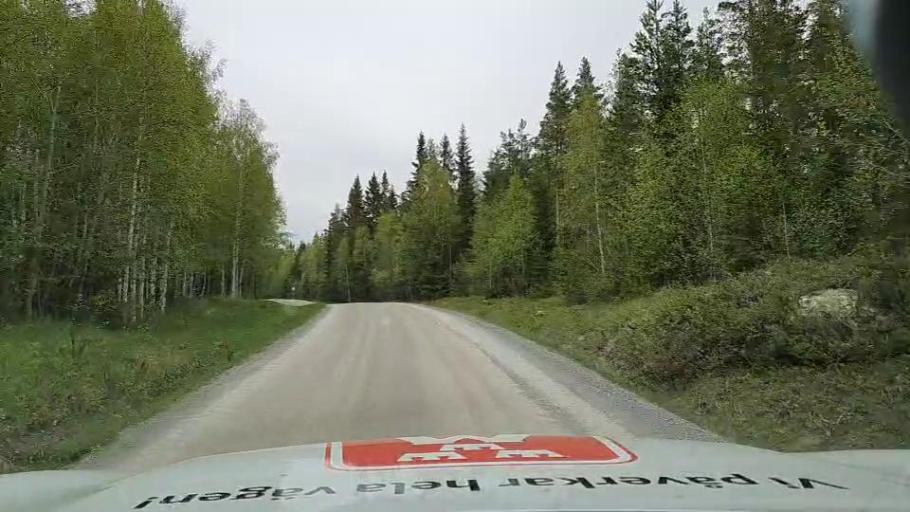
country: SE
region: Jaemtland
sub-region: OEstersunds Kommun
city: Brunflo
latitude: 62.9360
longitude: 14.6634
